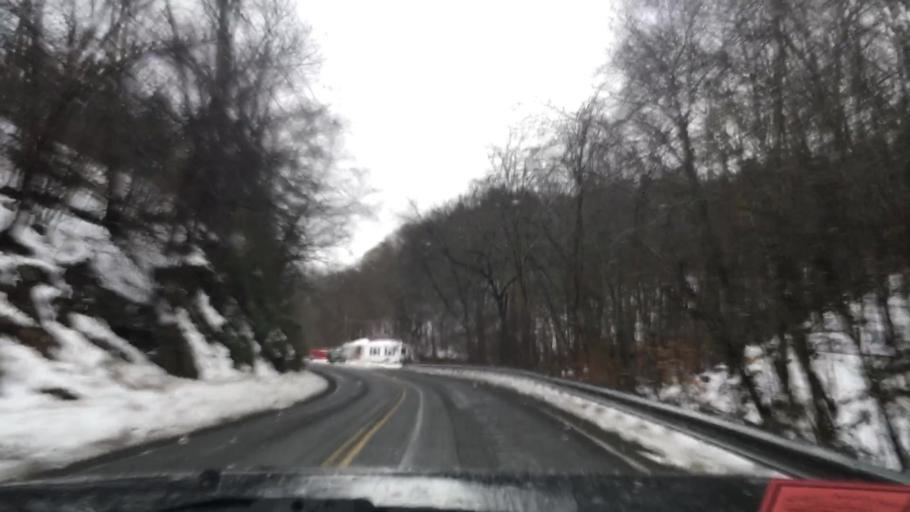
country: US
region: Virginia
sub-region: Pulaski County
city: Pulaski
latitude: 37.0126
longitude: -80.7002
